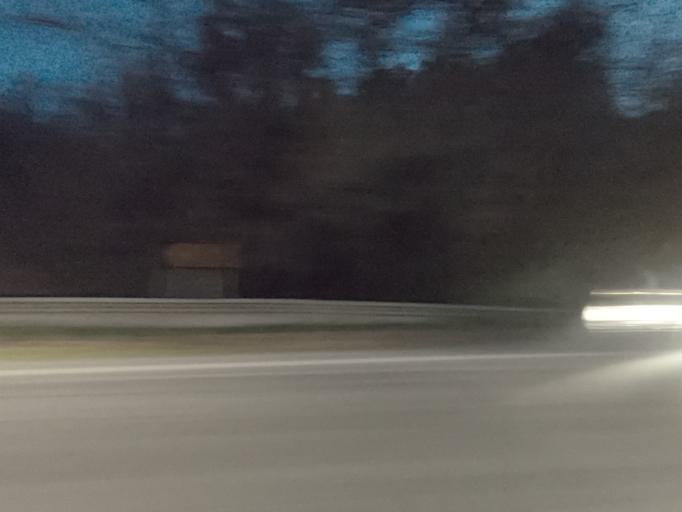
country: PT
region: Porto
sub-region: Amarante
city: Amarante
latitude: 41.2359
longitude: -8.0242
